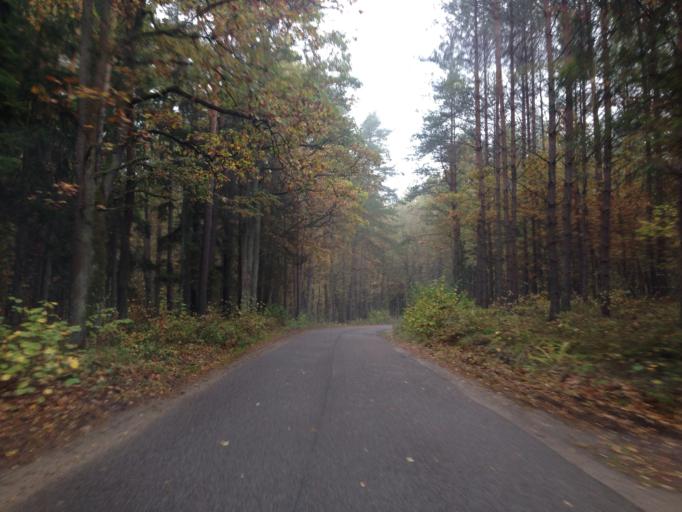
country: PL
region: Warmian-Masurian Voivodeship
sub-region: Powiat dzialdowski
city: Lidzbark
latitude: 53.2473
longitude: 19.7452
